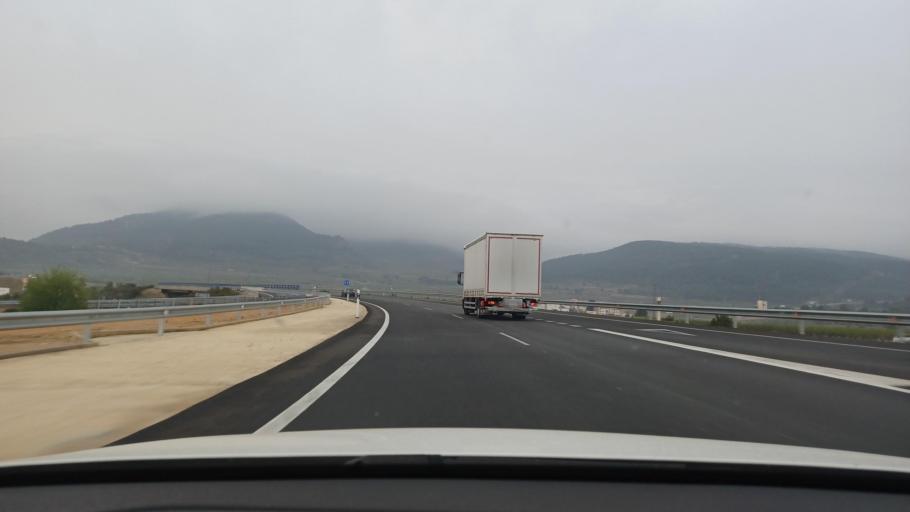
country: ES
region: Valencia
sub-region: Provincia de Valencia
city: La Font de la Figuera
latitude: 38.8292
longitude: -0.8918
